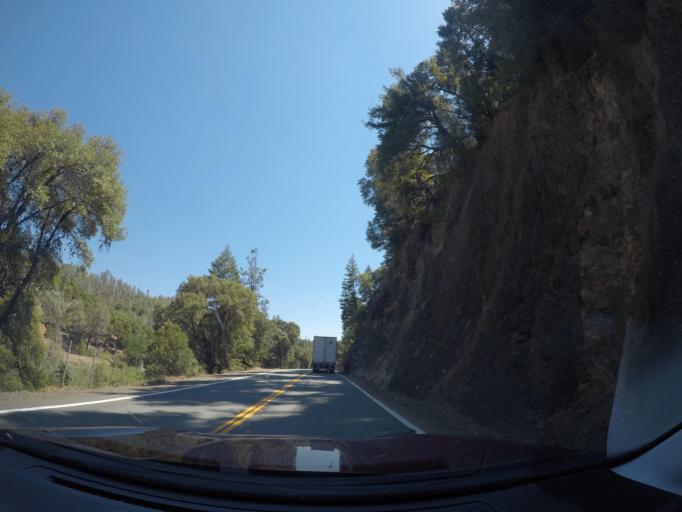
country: US
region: California
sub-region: Shasta County
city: Bella Vista
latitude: 40.7226
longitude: -122.0820
